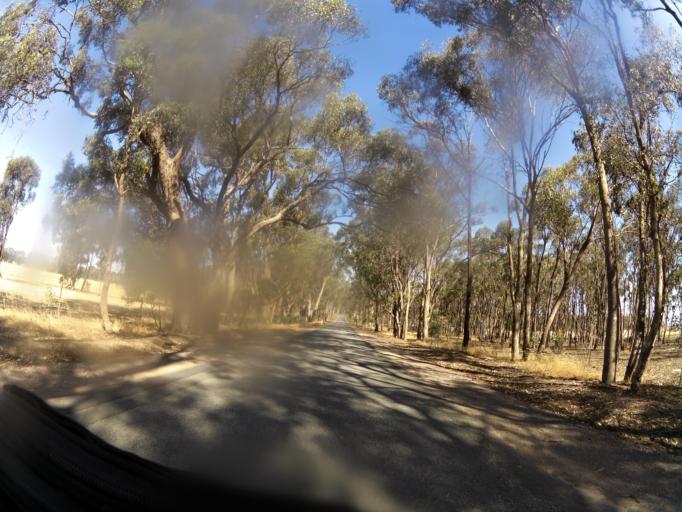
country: AU
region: Victoria
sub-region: Campaspe
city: Kyabram
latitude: -36.8800
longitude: 145.0903
